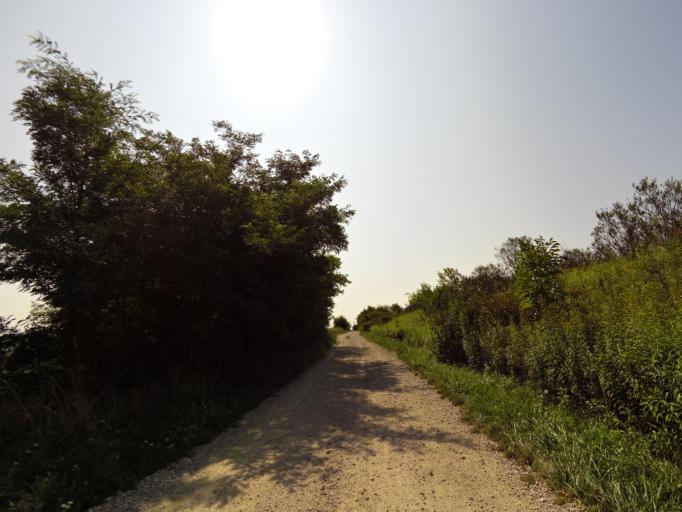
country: HU
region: Veszprem
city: Tapolca
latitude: 46.8345
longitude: 17.3653
